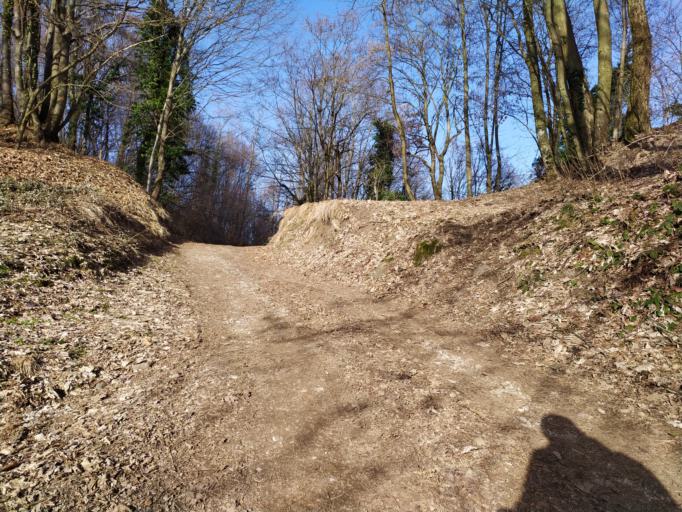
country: IT
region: Veneto
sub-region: Provincia di Vicenza
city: San Quirico
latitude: 45.6982
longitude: 11.2865
